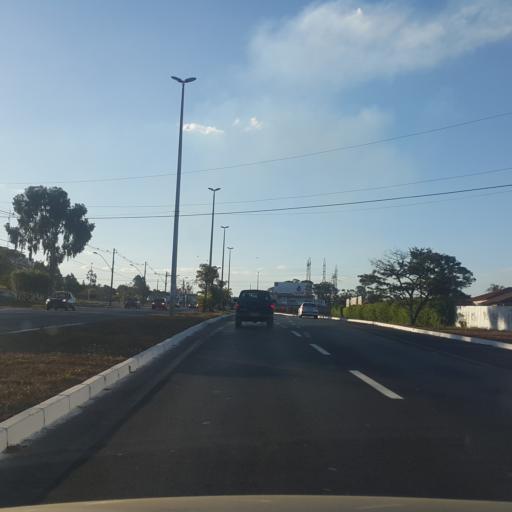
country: BR
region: Federal District
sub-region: Brasilia
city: Brasilia
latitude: -15.8401
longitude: -48.0026
